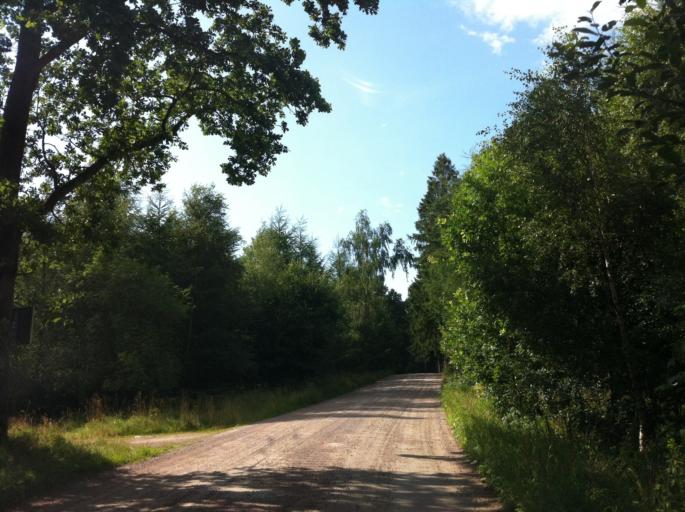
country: SE
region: Skane
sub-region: Astorps Kommun
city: Kvidinge
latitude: 56.1155
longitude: 13.0149
